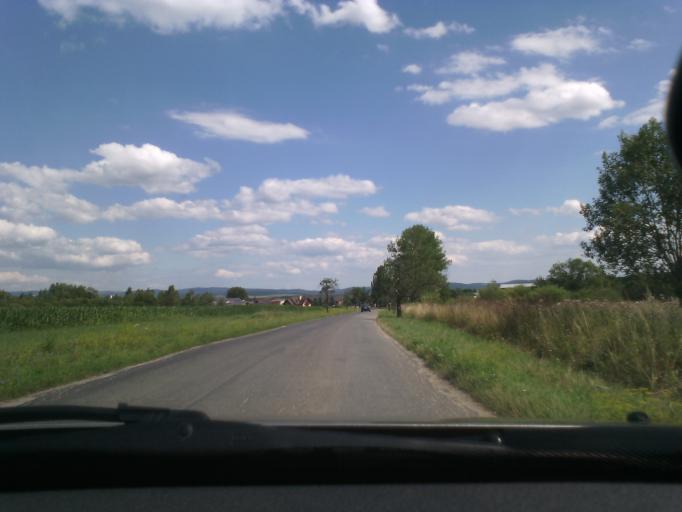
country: SK
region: Presovsky
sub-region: Okres Poprad
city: Poprad
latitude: 49.1217
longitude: 20.3448
